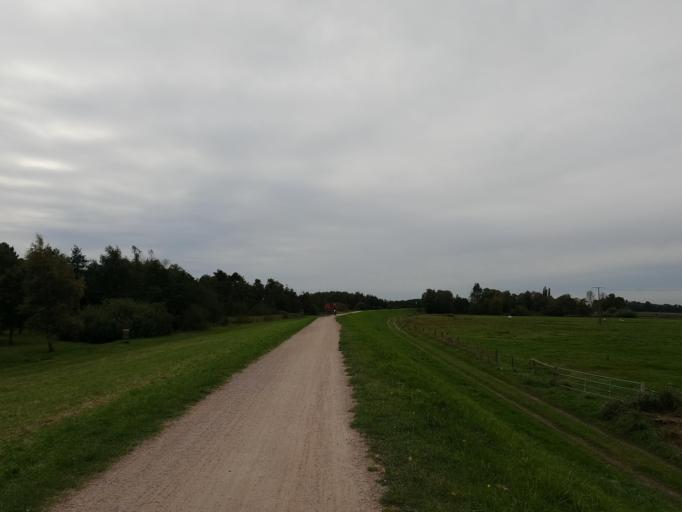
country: DE
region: Schleswig-Holstein
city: Kellenhusen
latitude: 54.1805
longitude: 11.0510
